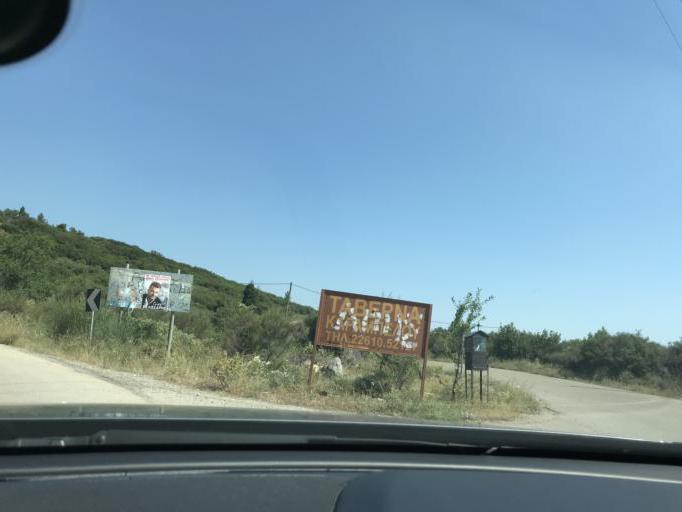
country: GR
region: Central Greece
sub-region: Nomos Fthiotidos
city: Kato Tithorea
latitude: 38.5123
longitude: 22.7223
